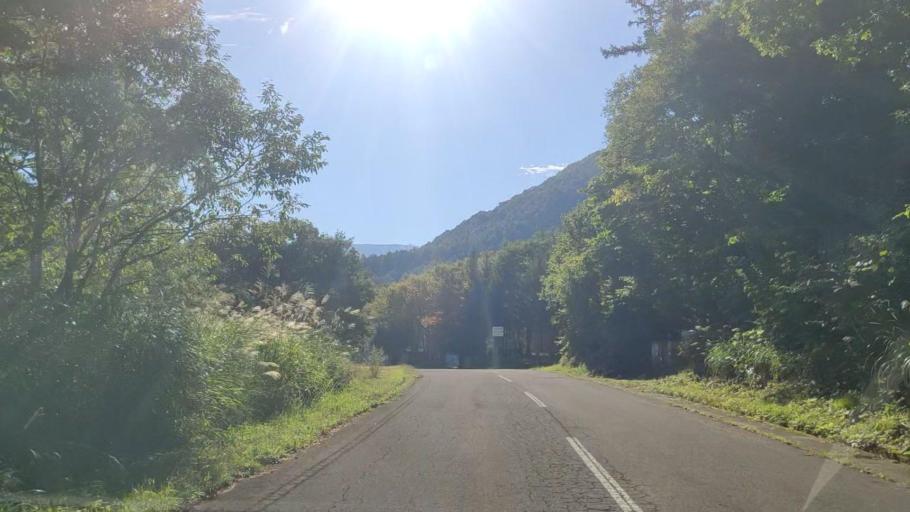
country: JP
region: Nagano
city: Iiyama
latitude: 36.8100
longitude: 138.4135
